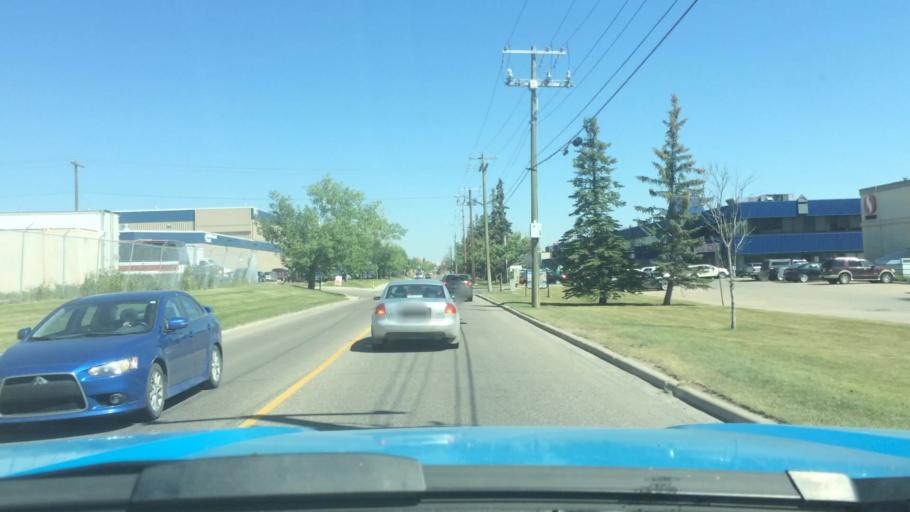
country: CA
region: Alberta
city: Calgary
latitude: 51.0539
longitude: -113.9859
